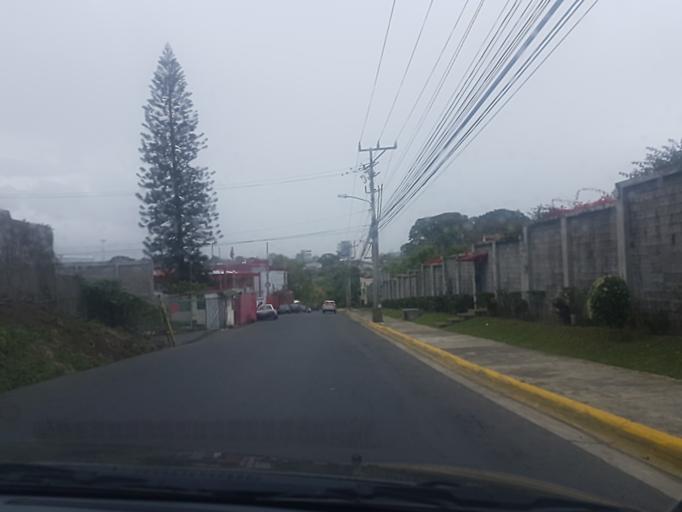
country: CR
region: San Jose
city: Calle Blancos
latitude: 9.9486
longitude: -84.0753
